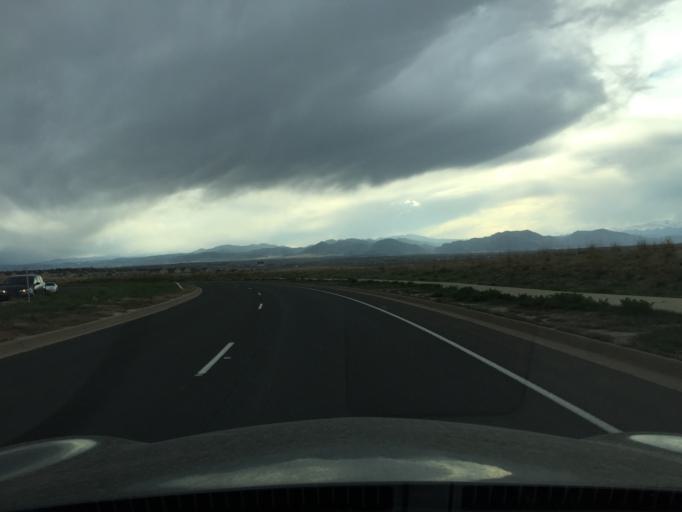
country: US
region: Colorado
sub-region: Boulder County
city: Lafayette
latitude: 39.9783
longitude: -105.0368
